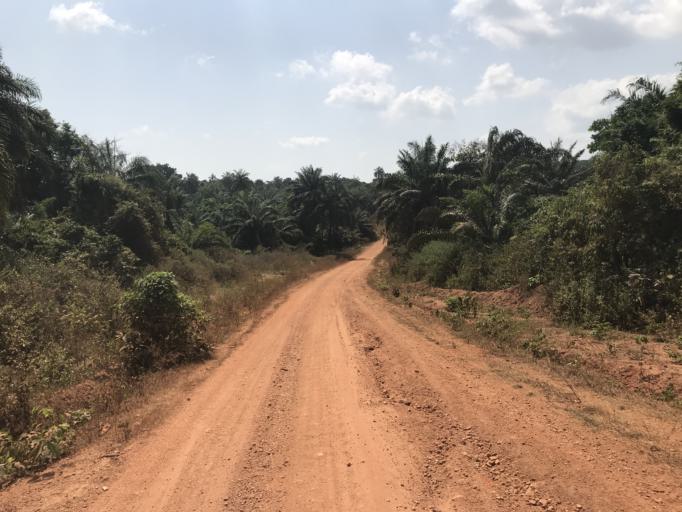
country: NG
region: Osun
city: Ifon
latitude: 7.9643
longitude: 4.5004
